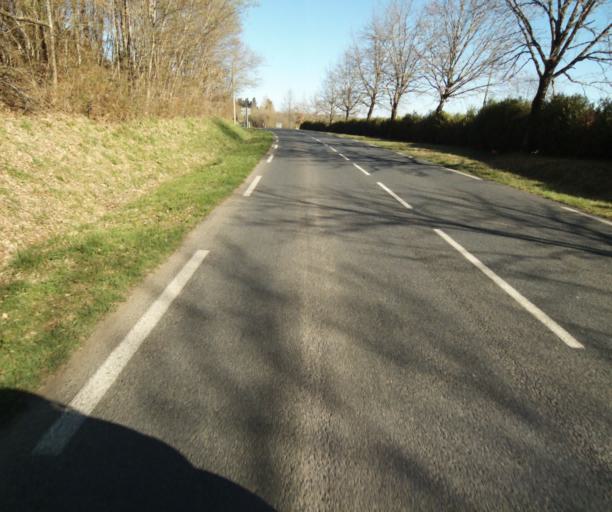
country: FR
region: Limousin
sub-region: Departement de la Correze
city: Chamboulive
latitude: 45.4048
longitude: 1.7211
